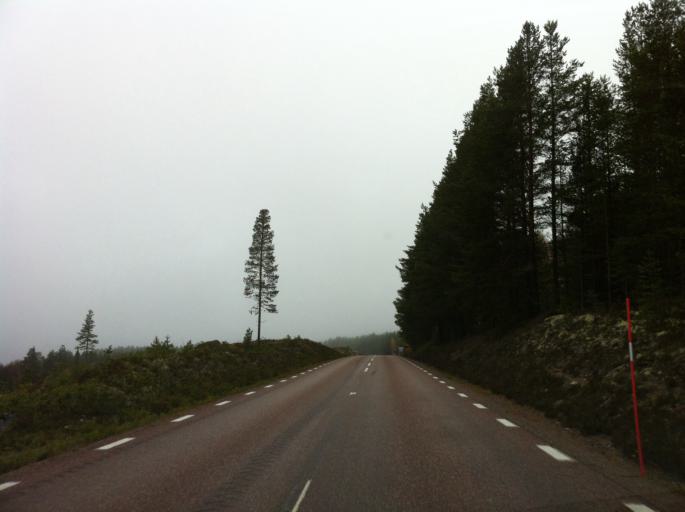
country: NO
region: Hedmark
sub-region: Trysil
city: Innbygda
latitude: 61.8492
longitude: 12.7645
